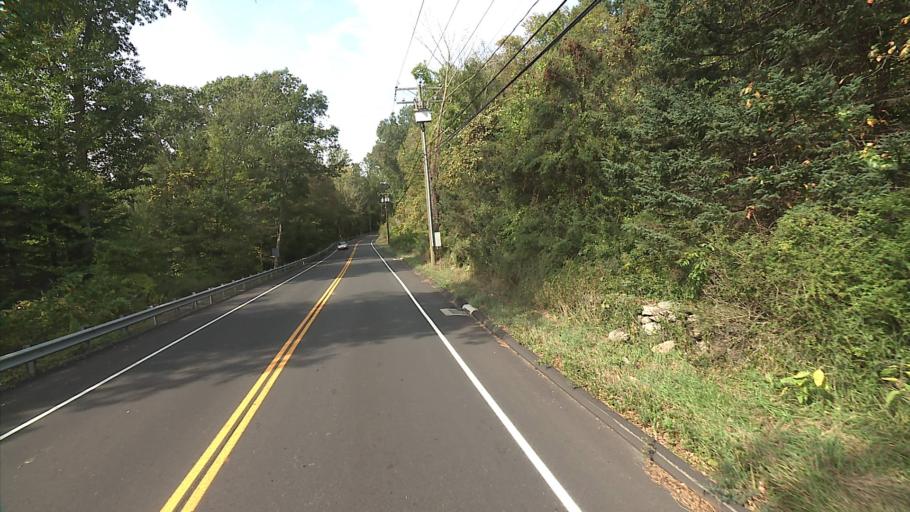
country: US
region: Connecticut
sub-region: New Haven County
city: Oxford
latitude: 41.3891
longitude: -73.1931
